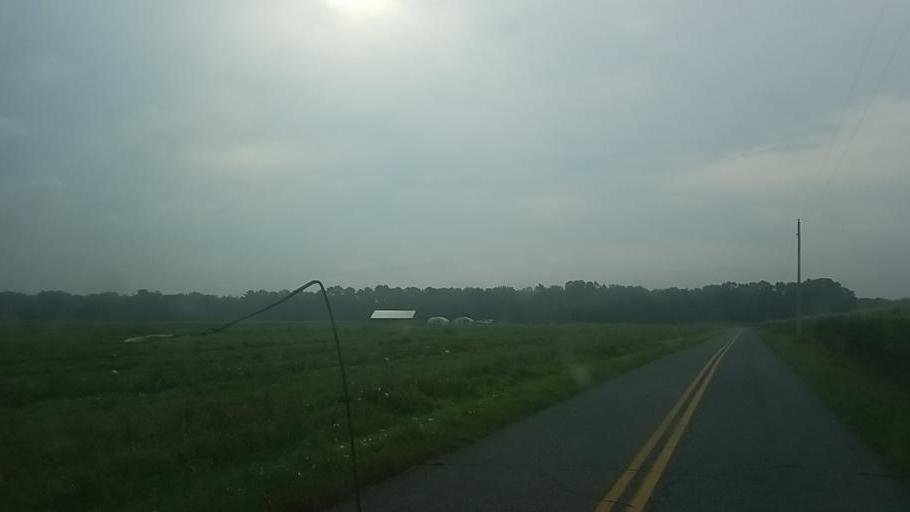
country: US
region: Maryland
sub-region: Wicomico County
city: Pittsville
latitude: 38.4344
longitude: -75.3266
